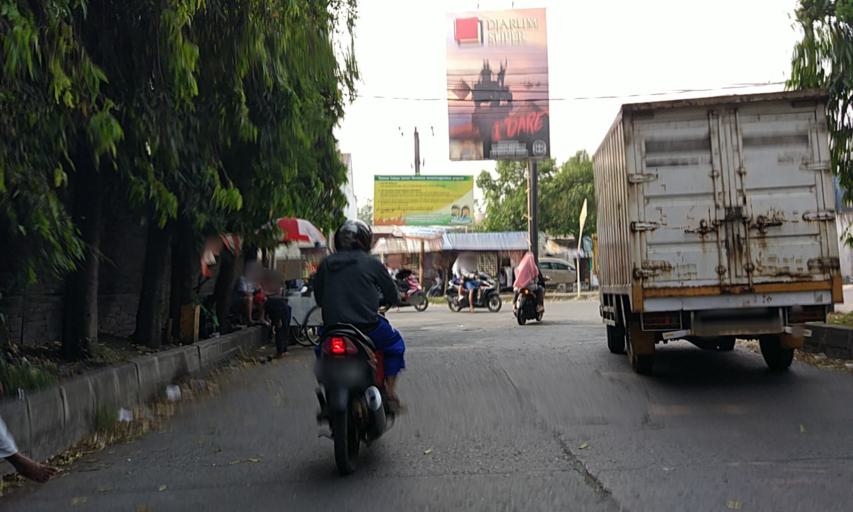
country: ID
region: West Java
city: Margahayukencana
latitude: -6.9529
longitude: 107.5629
